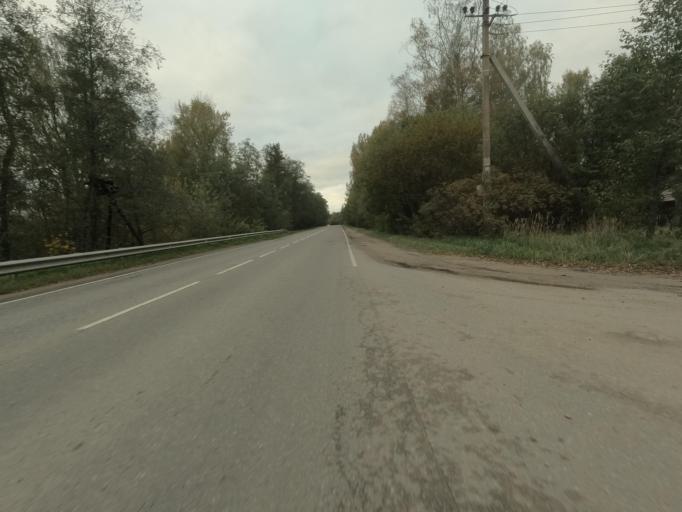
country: RU
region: Leningrad
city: Pavlovo
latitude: 59.7833
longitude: 30.9705
